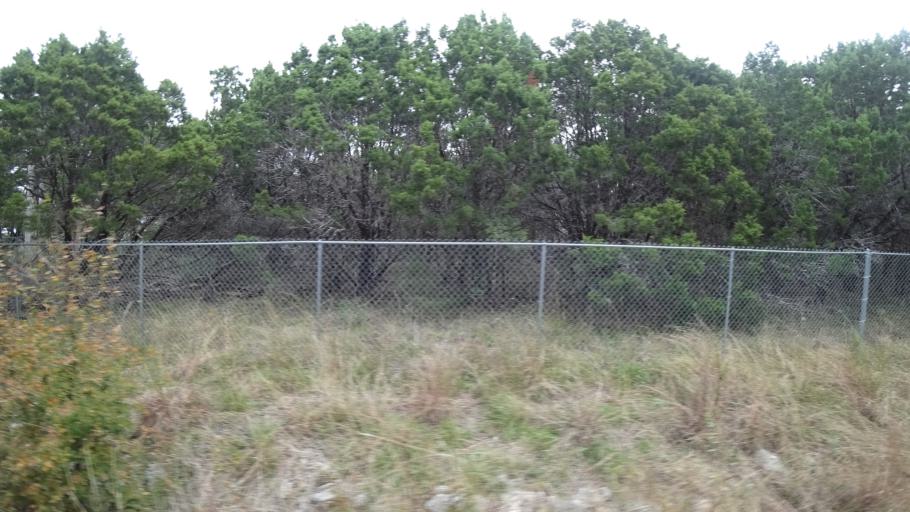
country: US
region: Texas
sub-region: Williamson County
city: Anderson Mill
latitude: 30.4508
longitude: -97.8381
